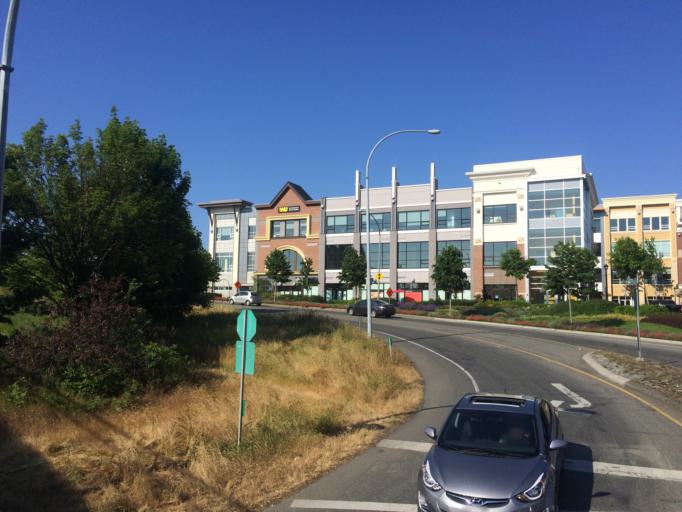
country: CA
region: British Columbia
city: Victoria
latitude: 48.4551
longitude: -123.3774
